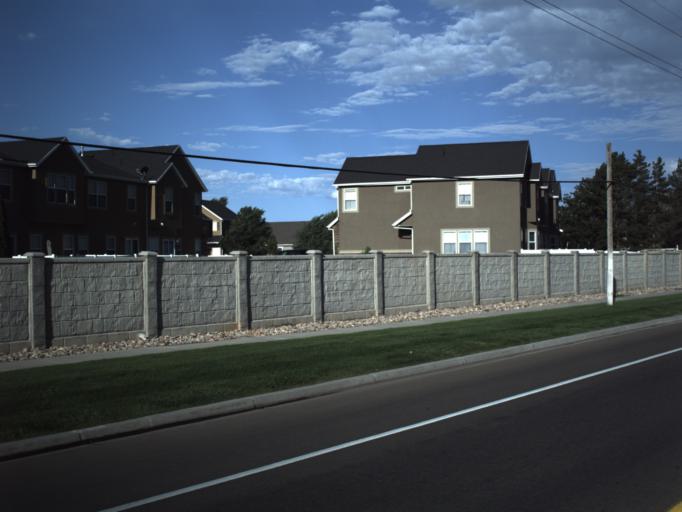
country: US
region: Utah
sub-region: Utah County
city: Spanish Fork
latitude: 40.0983
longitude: -111.6242
